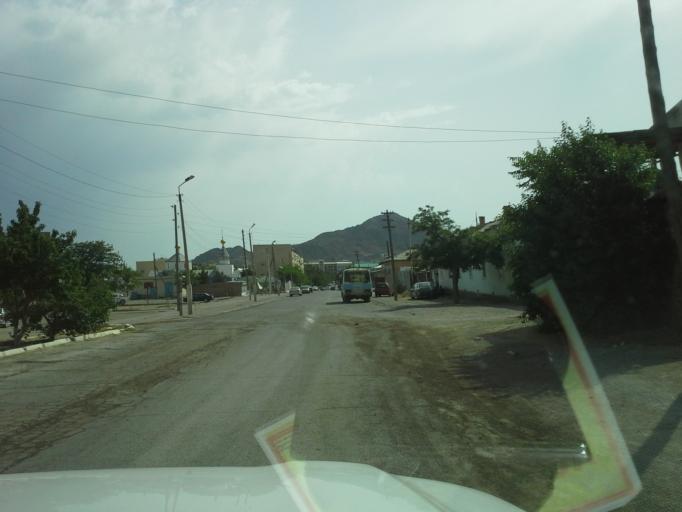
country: TM
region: Balkan
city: Turkmenbasy
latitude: 40.0098
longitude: 53.0005
